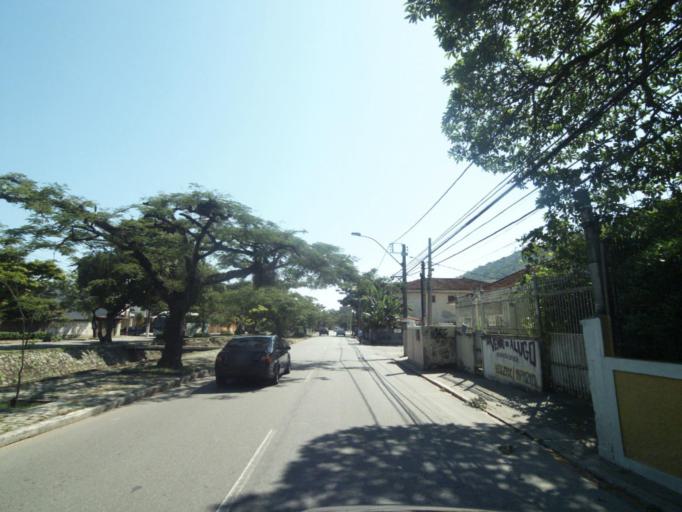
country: BR
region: Rio de Janeiro
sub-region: Niteroi
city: Niteroi
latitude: -22.9138
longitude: -43.0834
